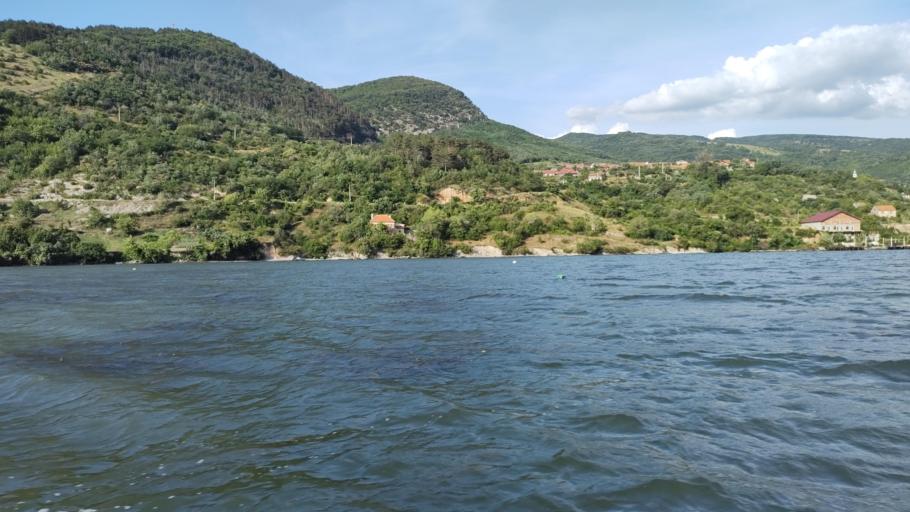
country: RO
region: Mehedinti
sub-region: Comuna Svinita
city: Svinita
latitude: 44.4990
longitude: 22.0904
